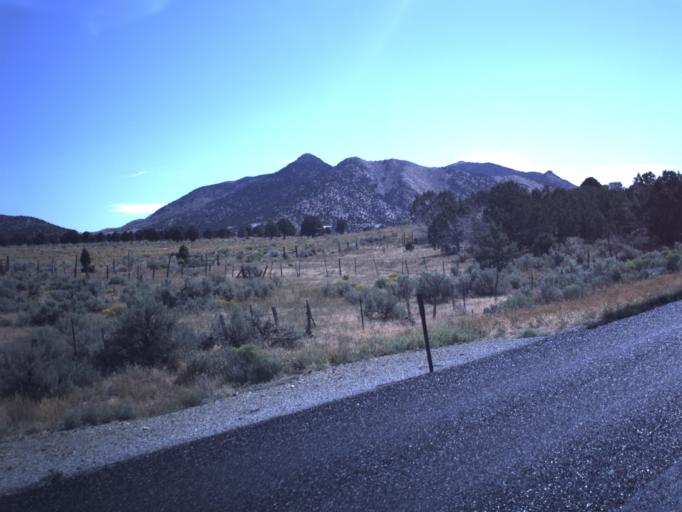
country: US
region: Utah
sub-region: Utah County
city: Genola
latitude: 39.9365
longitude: -112.1784
